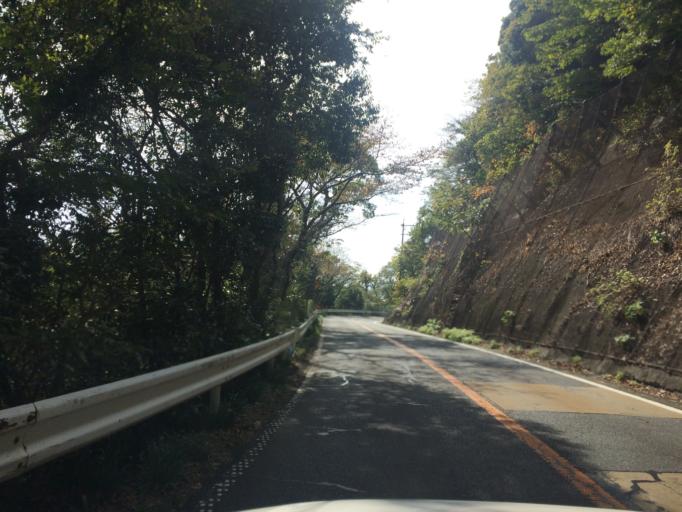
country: JP
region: Shizuoka
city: Yaizu
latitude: 34.8838
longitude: 138.3343
